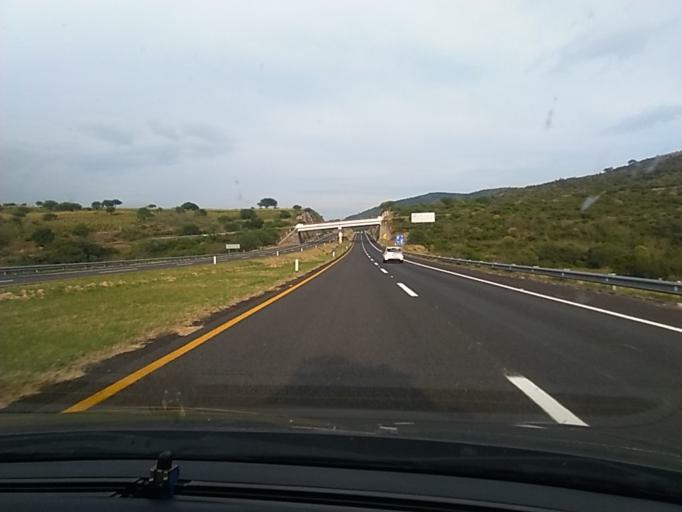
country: MX
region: Michoacan
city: Copandaro de Galeana
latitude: 19.8913
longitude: -101.1700
